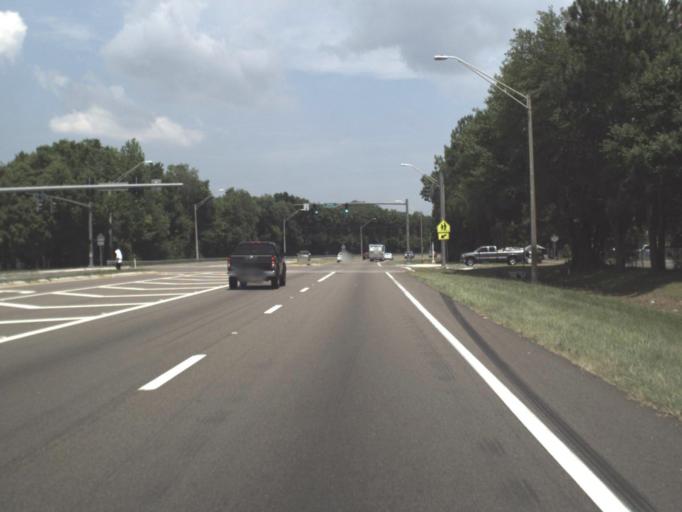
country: US
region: Florida
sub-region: Duval County
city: Jacksonville
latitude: 30.3568
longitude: -81.6873
